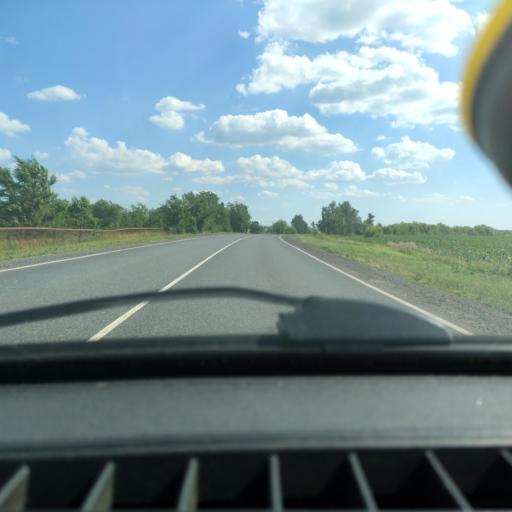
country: RU
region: Samara
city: Povolzhskiy
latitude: 53.7002
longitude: 49.7424
